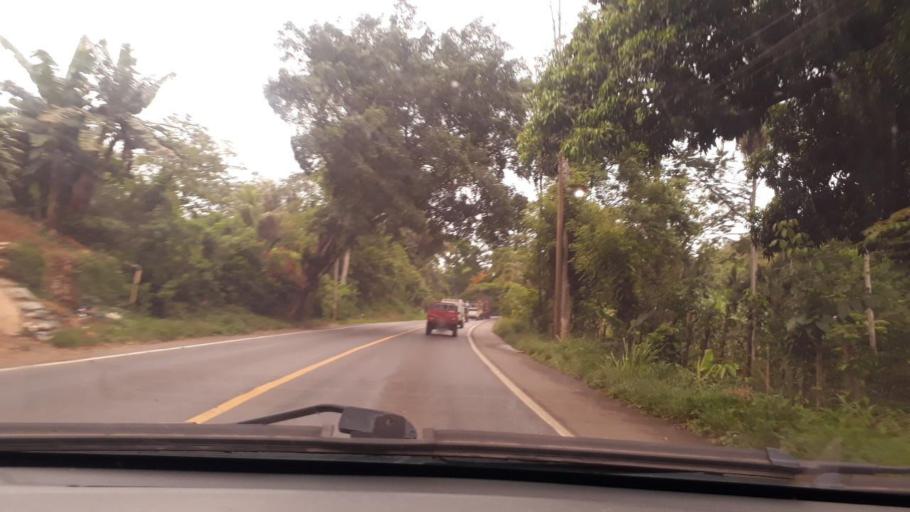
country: GT
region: Izabal
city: Morales
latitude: 15.5379
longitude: -88.7537
